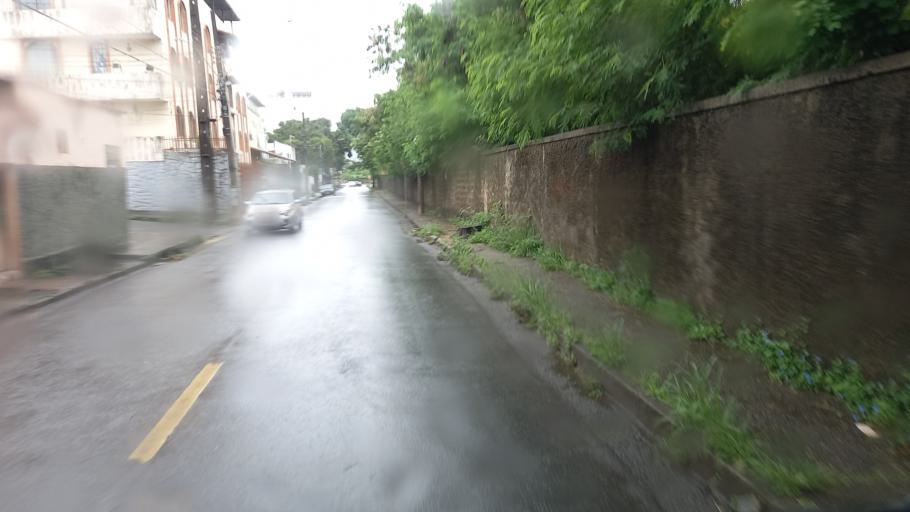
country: BR
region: Minas Gerais
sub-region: Belo Horizonte
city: Belo Horizonte
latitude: -19.8925
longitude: -43.9113
